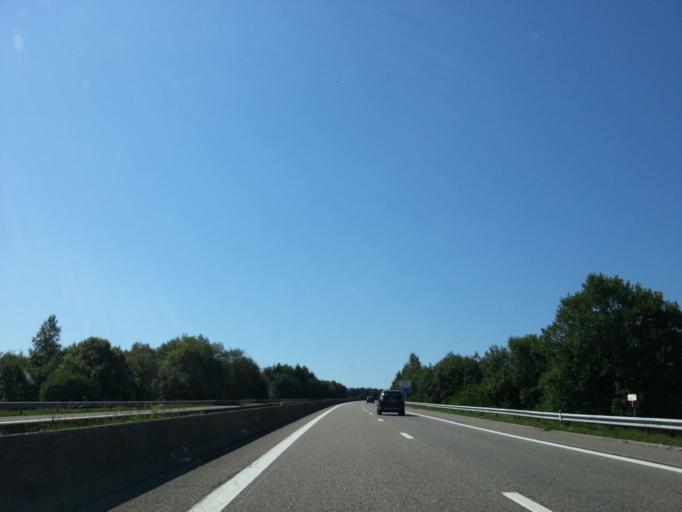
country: BE
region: Wallonia
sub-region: Province de Liege
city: Saint-Vith
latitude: 50.3304
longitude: 6.0907
